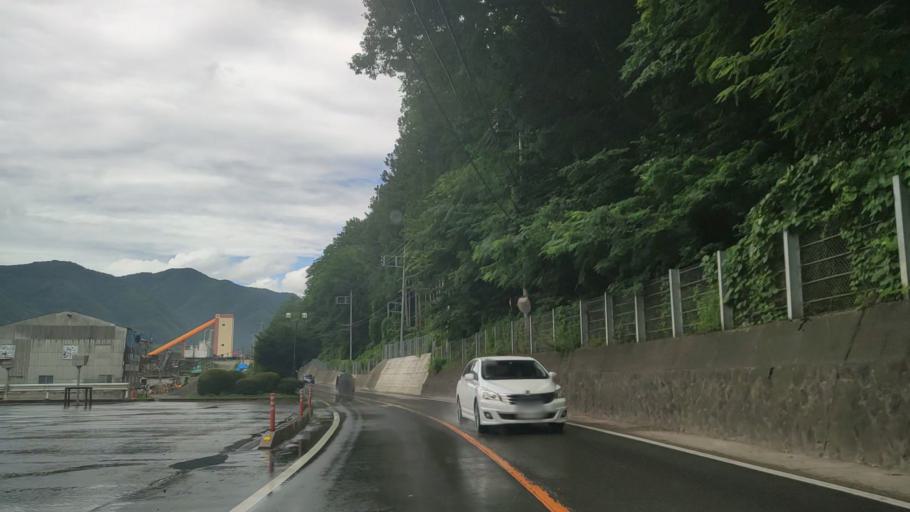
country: JP
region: Gunma
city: Numata
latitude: 36.7486
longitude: 139.2334
